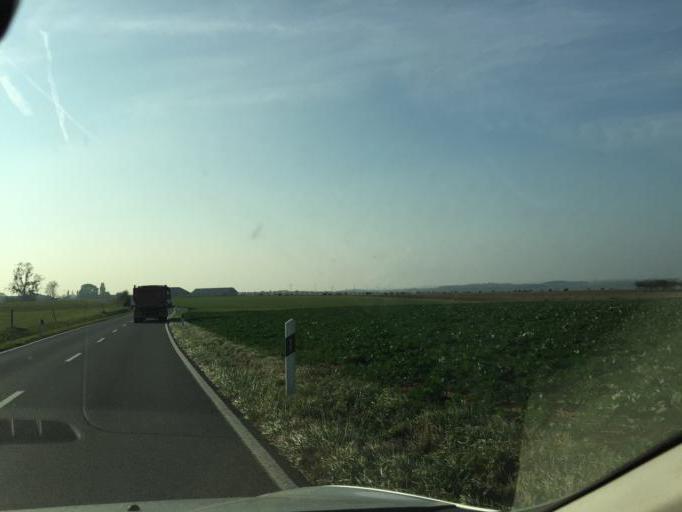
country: LU
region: Grevenmacher
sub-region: Canton de Remich
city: Dalheim
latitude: 49.5410
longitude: 6.2393
